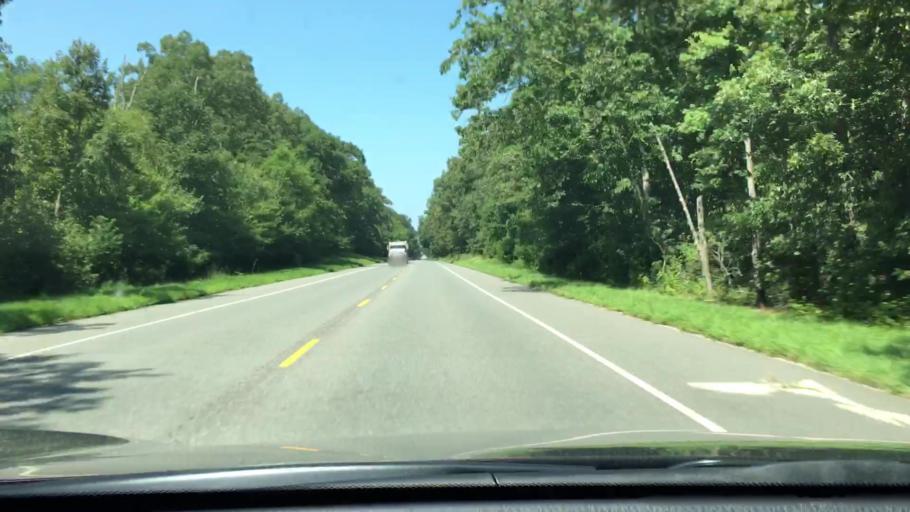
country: US
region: New Jersey
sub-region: Cumberland County
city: Laurel Lake
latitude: 39.3459
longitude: -75.0437
